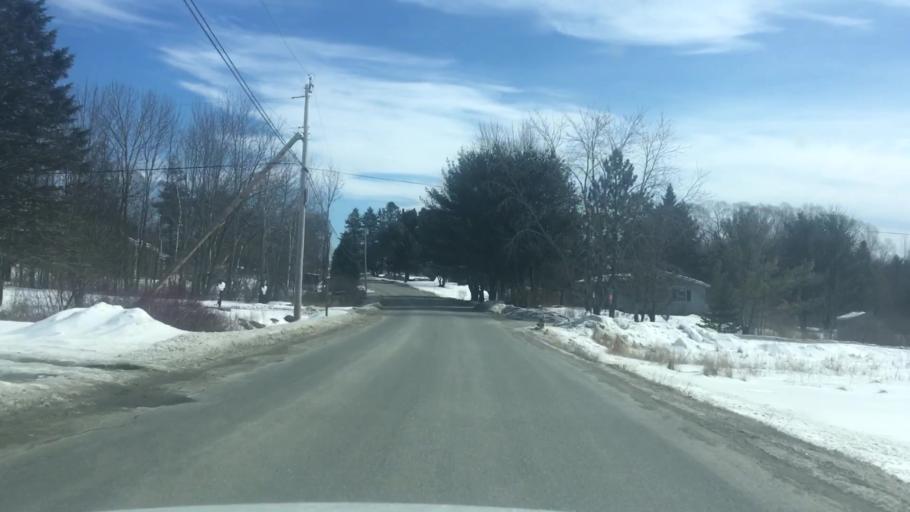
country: US
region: Maine
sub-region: Penobscot County
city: Eddington
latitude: 44.7986
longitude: -68.6777
